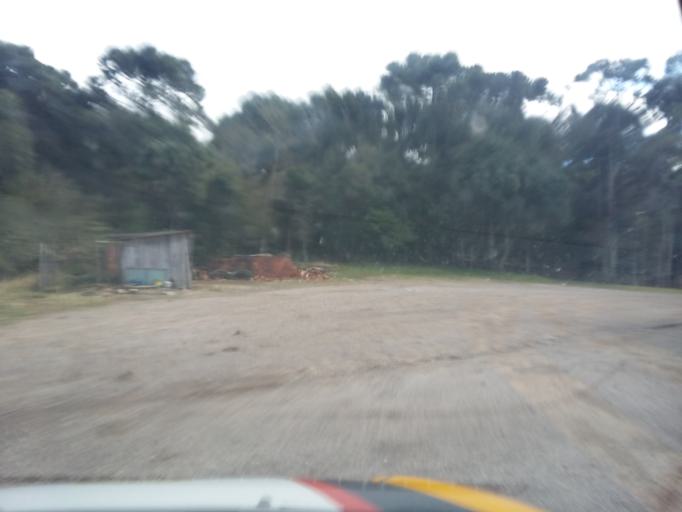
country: BR
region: Rio Grande do Sul
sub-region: Sao Marcos
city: Sao Marcos
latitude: -28.7811
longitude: -51.0971
